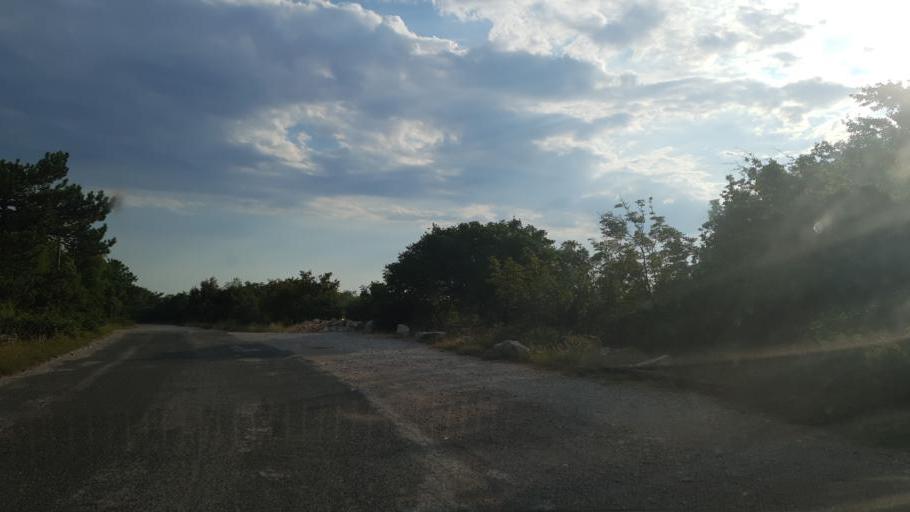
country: HR
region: Primorsko-Goranska
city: Omisalj
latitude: 45.2280
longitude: 14.5736
